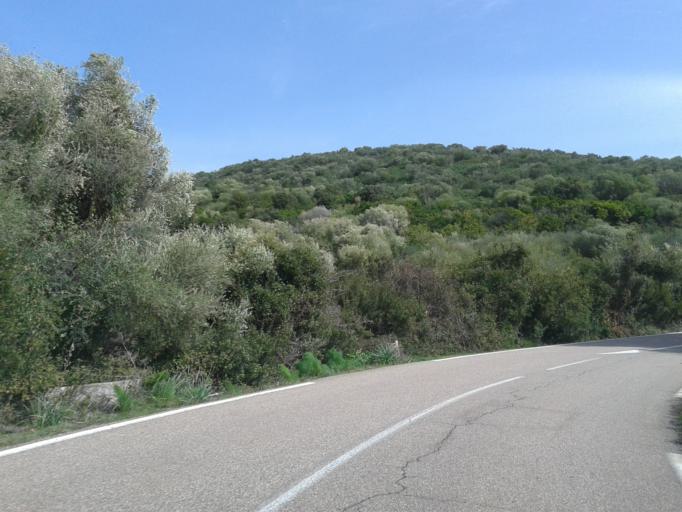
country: FR
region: Corsica
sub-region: Departement de la Haute-Corse
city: Monticello
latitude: 42.6479
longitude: 9.0987
